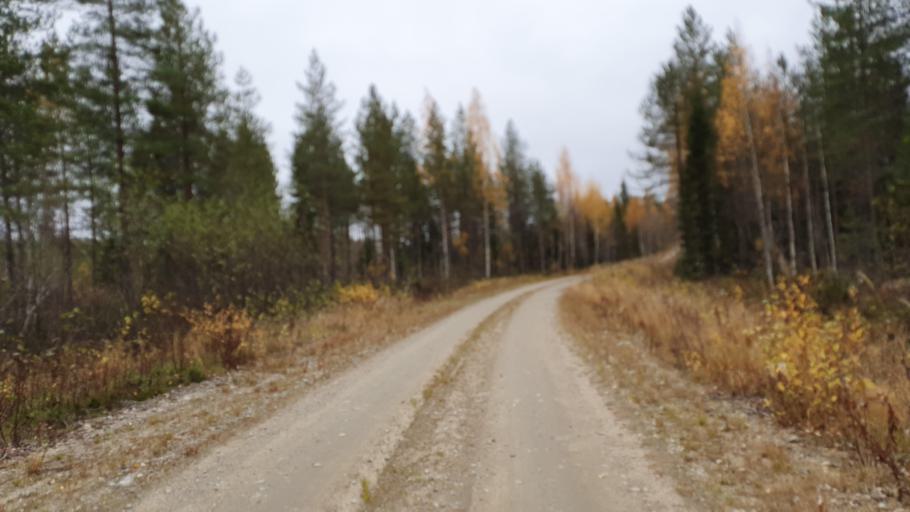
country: FI
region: Kainuu
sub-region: Kehys-Kainuu
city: Kuhmo
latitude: 64.4441
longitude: 29.6138
